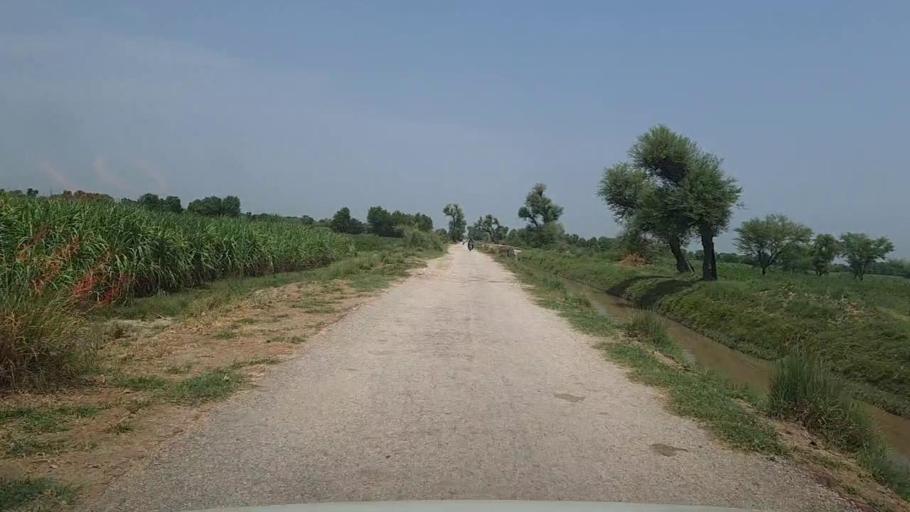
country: PK
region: Sindh
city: Karaundi
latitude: 26.8885
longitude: 68.3335
